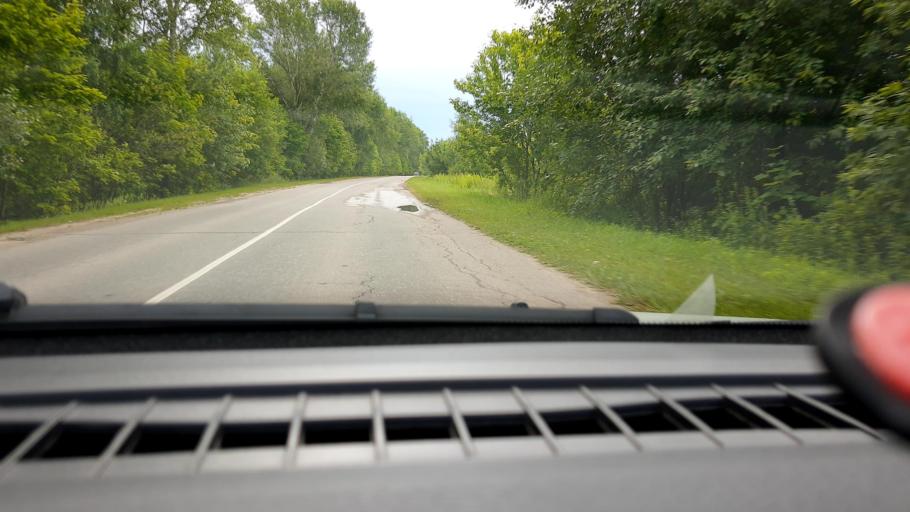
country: RU
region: Nizjnij Novgorod
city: Kstovo
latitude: 56.1486
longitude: 44.3201
